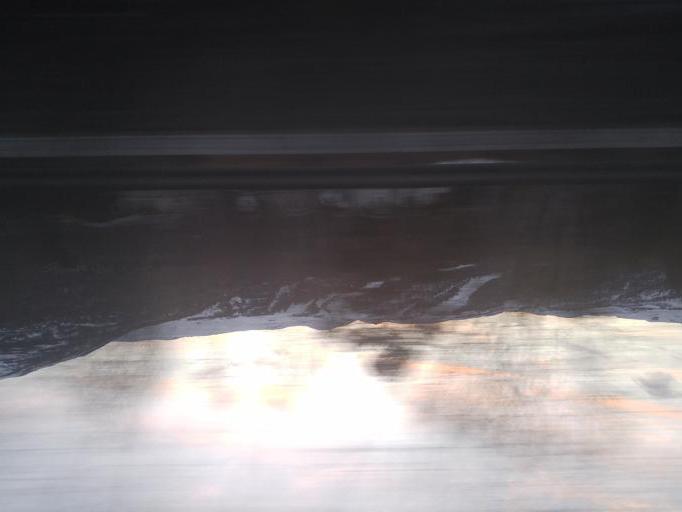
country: NO
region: Sor-Trondelag
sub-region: Oppdal
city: Oppdal
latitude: 62.6109
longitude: 9.7473
